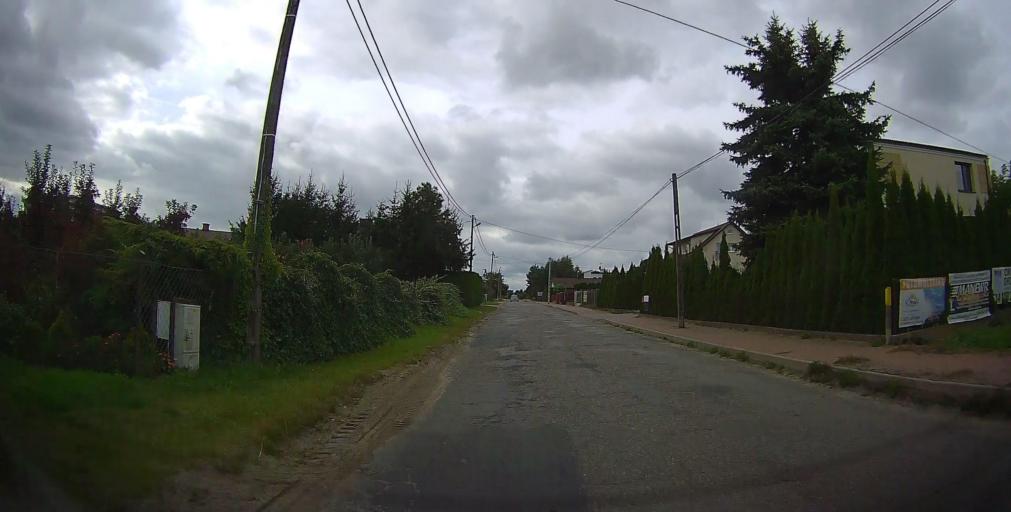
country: PL
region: Masovian Voivodeship
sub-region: Powiat grojecki
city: Belsk Duzy
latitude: 51.8163
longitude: 20.8269
